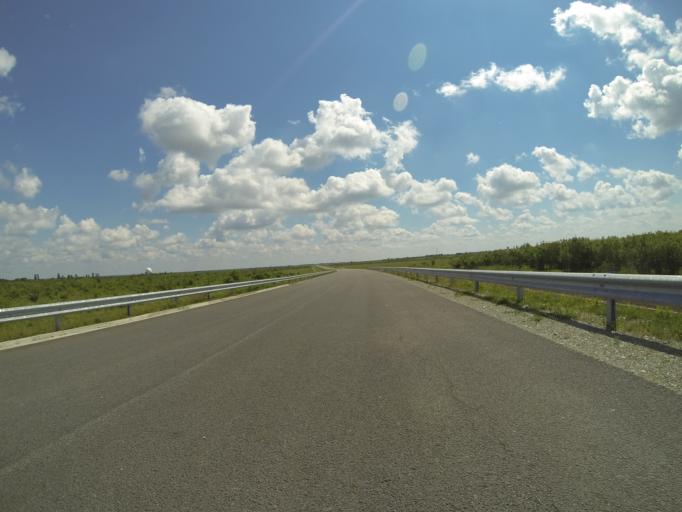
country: RO
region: Dolj
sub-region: Comuna Carcea
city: Carcea
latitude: 44.2837
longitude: 23.9062
